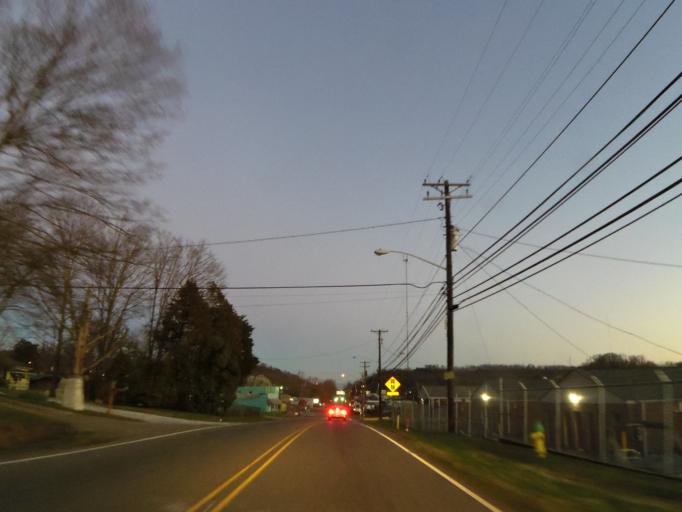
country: US
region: Tennessee
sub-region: Knox County
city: Knoxville
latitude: 36.0093
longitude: -83.9678
